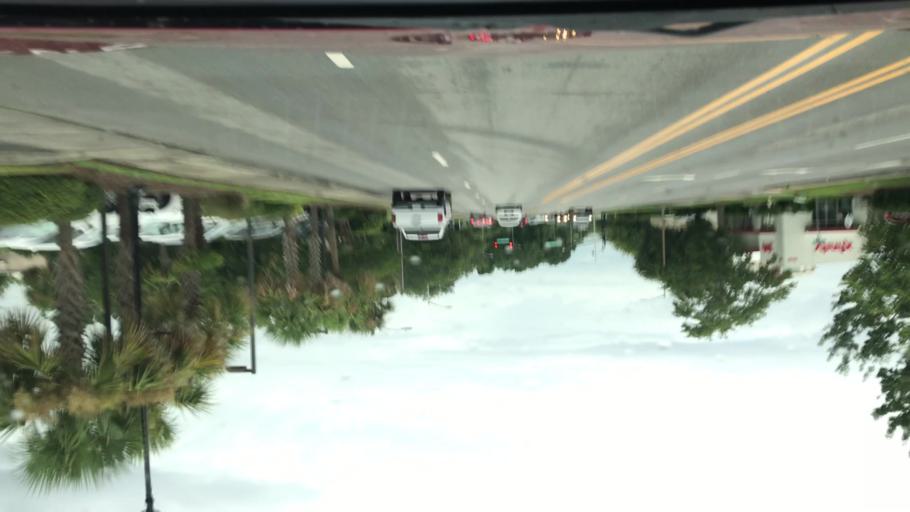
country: US
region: South Carolina
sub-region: Charleston County
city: North Charleston
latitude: 32.8661
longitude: -80.0145
